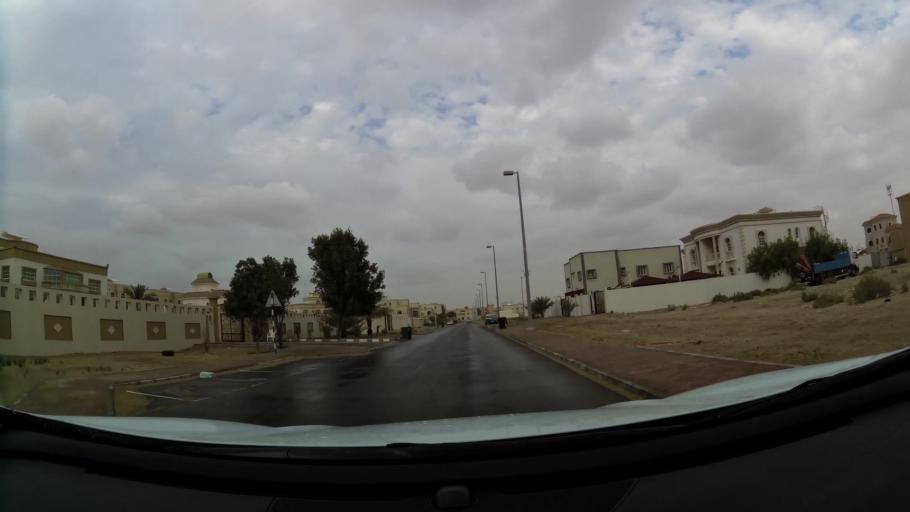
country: AE
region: Abu Dhabi
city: Abu Dhabi
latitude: 24.3569
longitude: 54.6294
